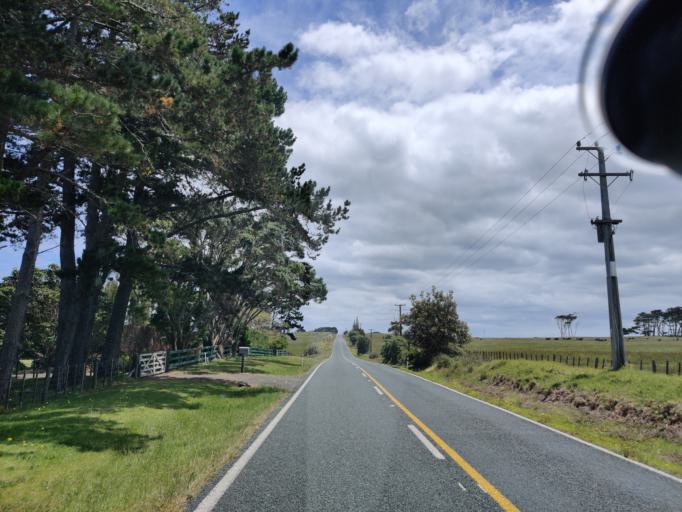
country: NZ
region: Northland
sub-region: Far North District
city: Kaitaia
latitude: -34.7050
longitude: 173.0310
